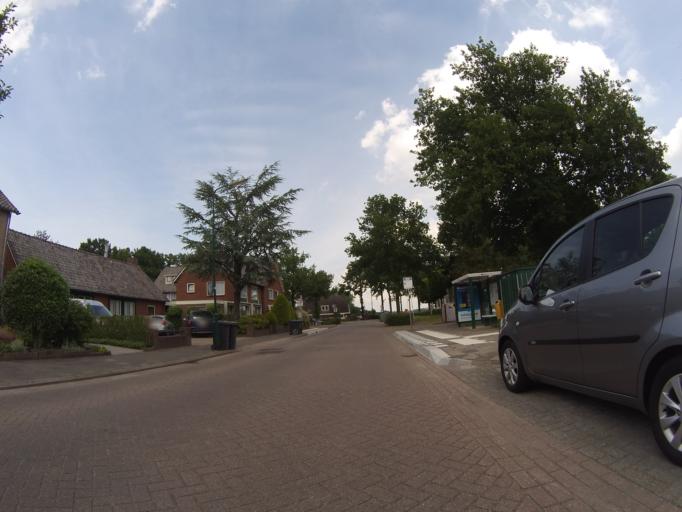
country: NL
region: Utrecht
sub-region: Gemeente De Bilt
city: De Bilt
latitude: 52.1575
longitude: 5.1828
